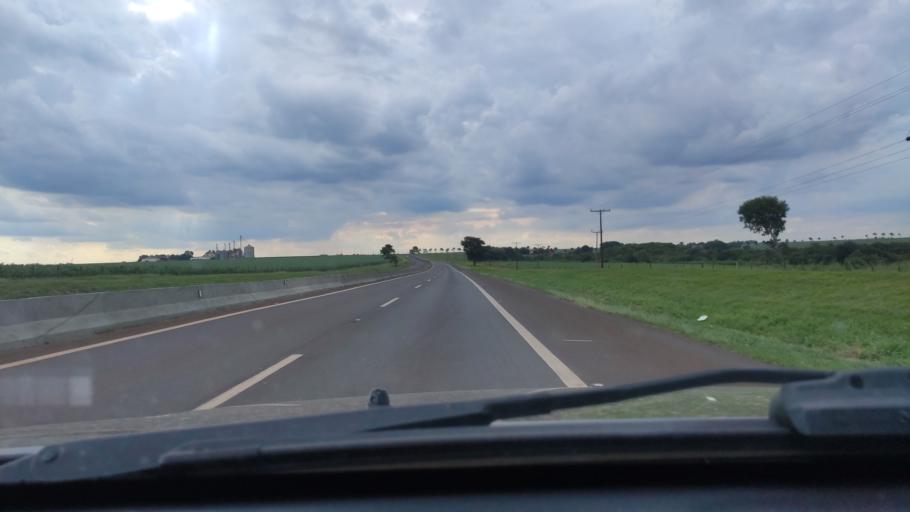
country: BR
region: Sao Paulo
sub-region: Palmital
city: Palmital
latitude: -22.8303
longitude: -50.0280
